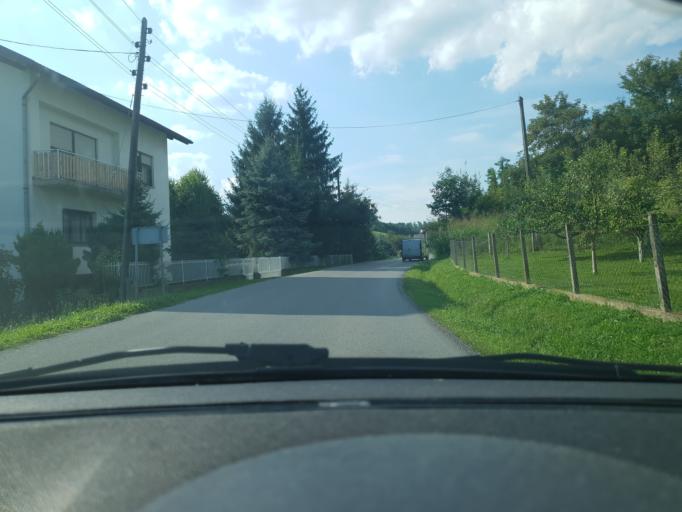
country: HR
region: Zagrebacka
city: Jakovlje
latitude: 46.0057
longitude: 15.8416
